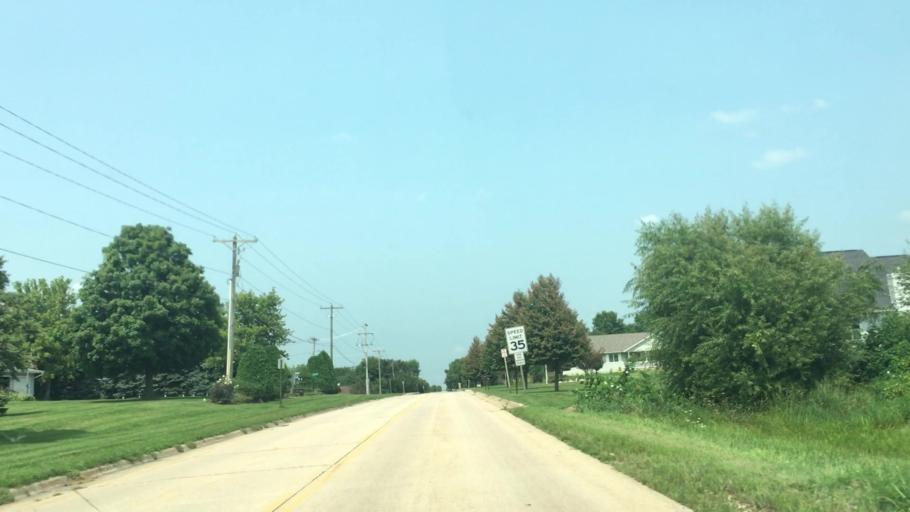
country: US
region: Iowa
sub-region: Fayette County
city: Oelwein
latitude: 42.6743
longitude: -91.8937
